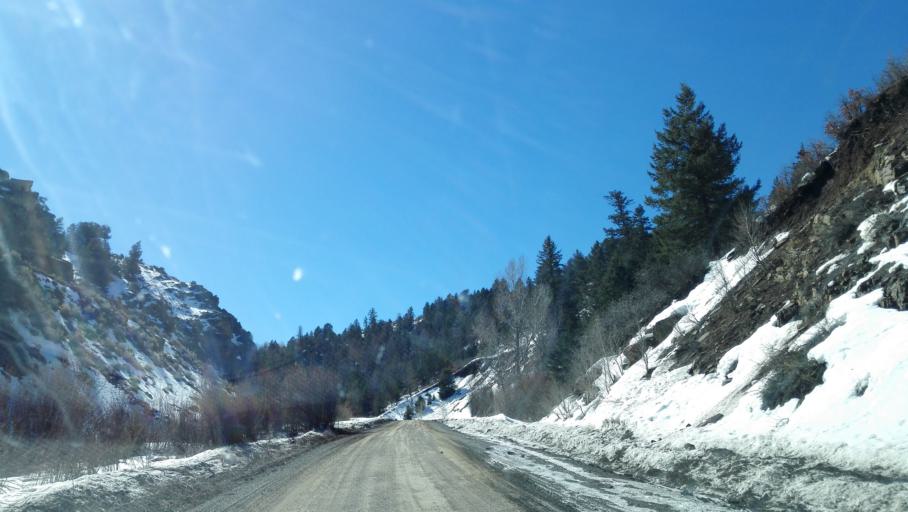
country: US
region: Colorado
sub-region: Hinsdale County
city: Lake City
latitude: 38.4459
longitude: -107.3442
